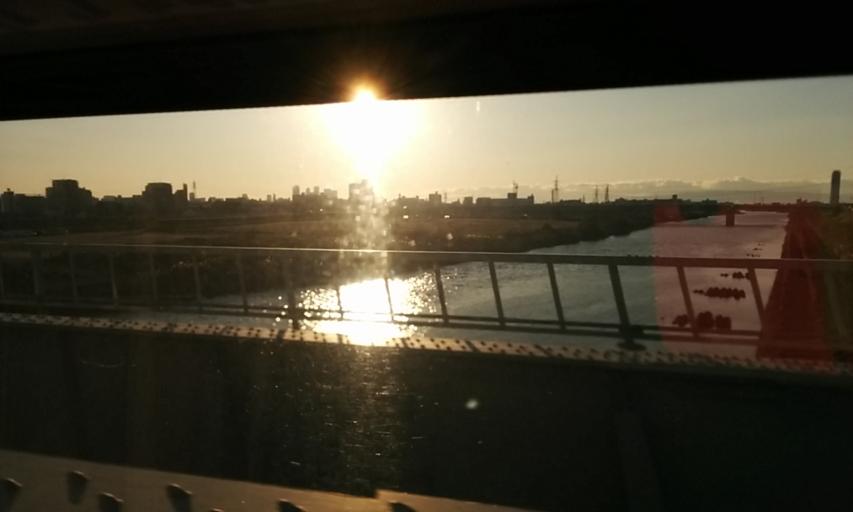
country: JP
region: Aichi
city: Kasugai
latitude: 35.2179
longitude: 136.9528
